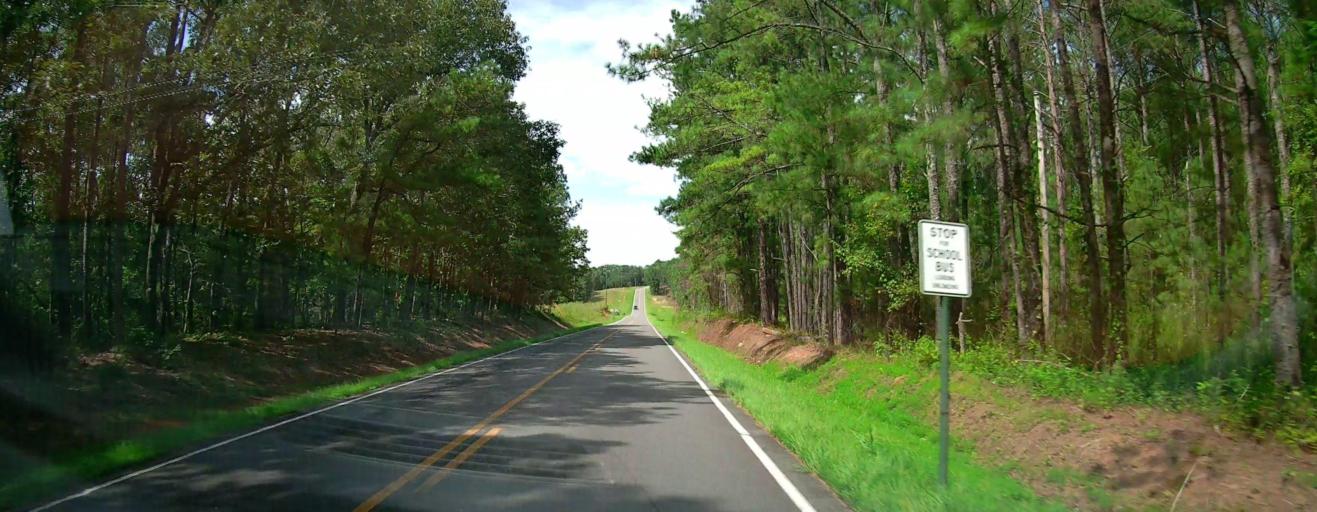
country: US
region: Georgia
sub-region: Taylor County
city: Butler
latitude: 32.5083
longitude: -84.2035
